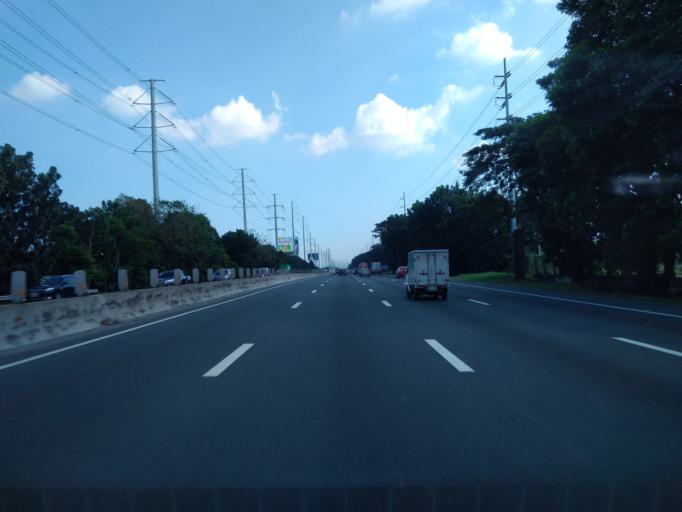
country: PH
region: Calabarzon
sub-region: Province of Cavite
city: Carmona
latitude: 14.3153
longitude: 121.0678
